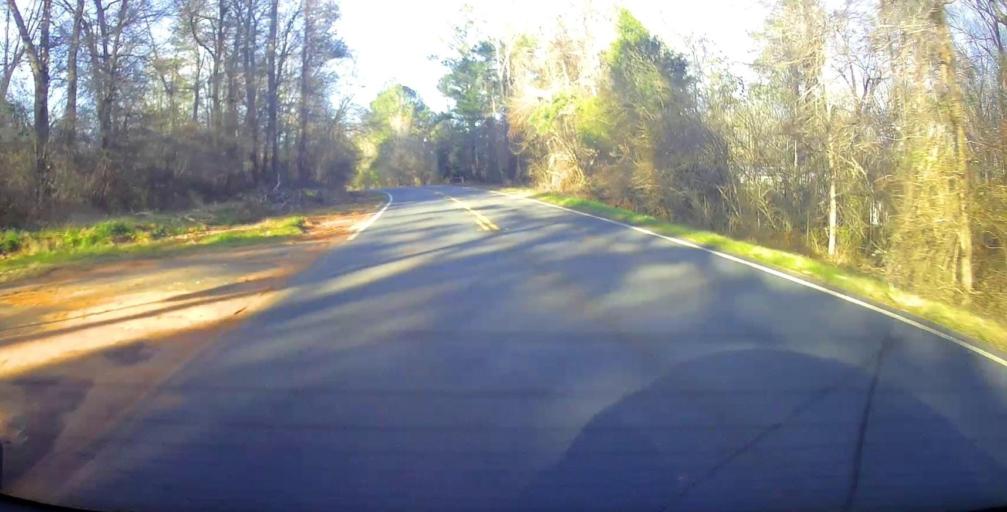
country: US
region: Georgia
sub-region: Harris County
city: Pine Mountain
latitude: 32.9082
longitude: -84.8032
